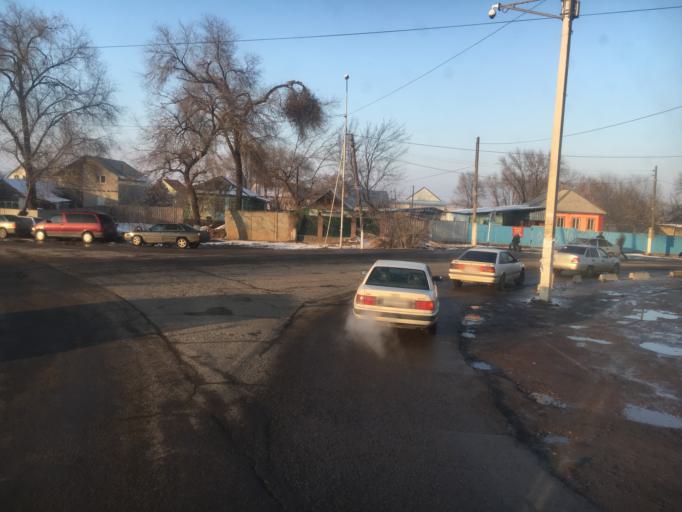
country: KZ
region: Almaty Oblysy
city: Burunday
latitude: 43.3771
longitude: 76.6418
